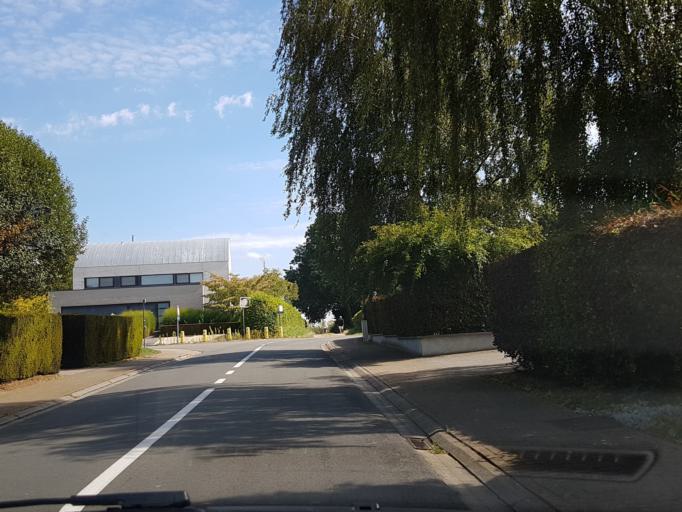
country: BE
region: Flanders
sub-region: Provincie Vlaams-Brabant
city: Herent
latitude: 50.8924
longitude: 4.6623
